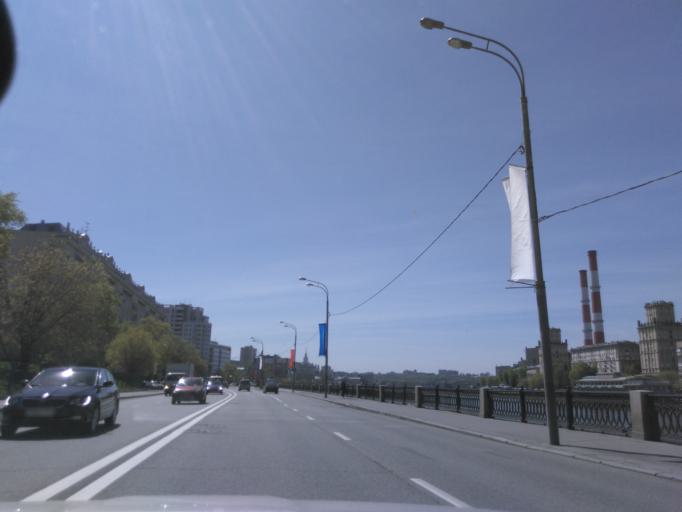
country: RU
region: Moskovskaya
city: Dorogomilovo
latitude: 55.7407
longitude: 37.5717
